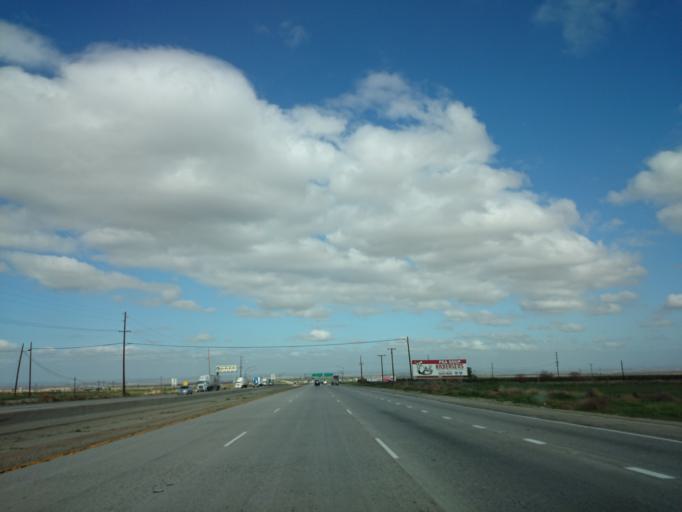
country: US
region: California
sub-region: Kern County
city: Frazier Park
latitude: 35.0027
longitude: -118.9503
